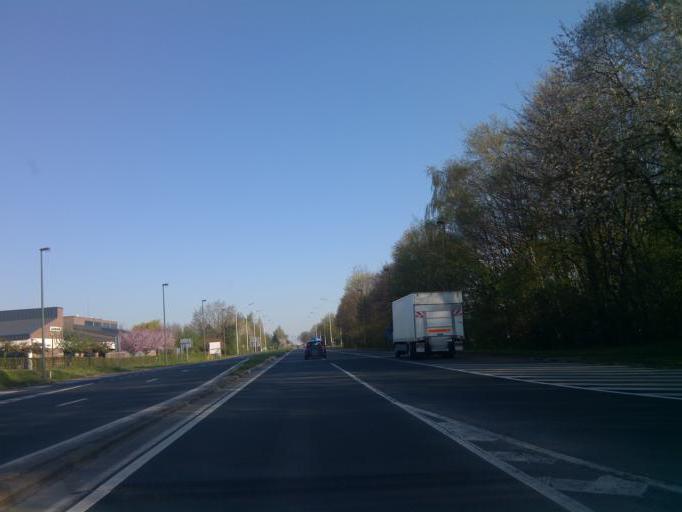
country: BE
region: Wallonia
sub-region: Province du Brabant Wallon
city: Louvain-la-Neuve
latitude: 50.6592
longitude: 4.6349
